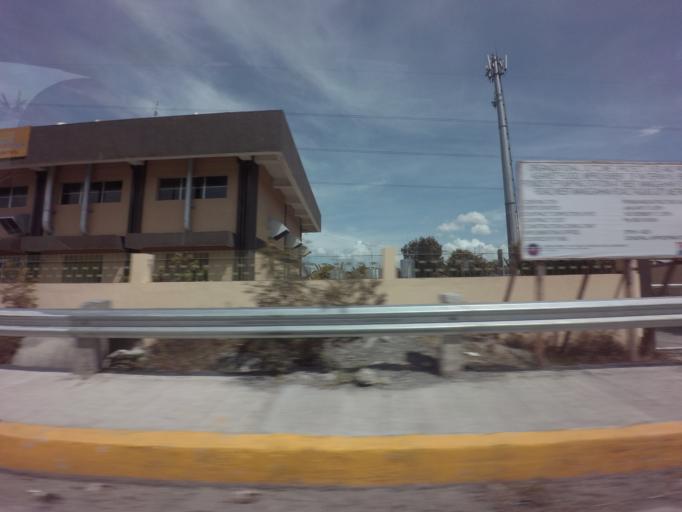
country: PH
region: Calabarzon
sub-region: Province of Rizal
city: Taguig
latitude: 14.5075
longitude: 121.0694
